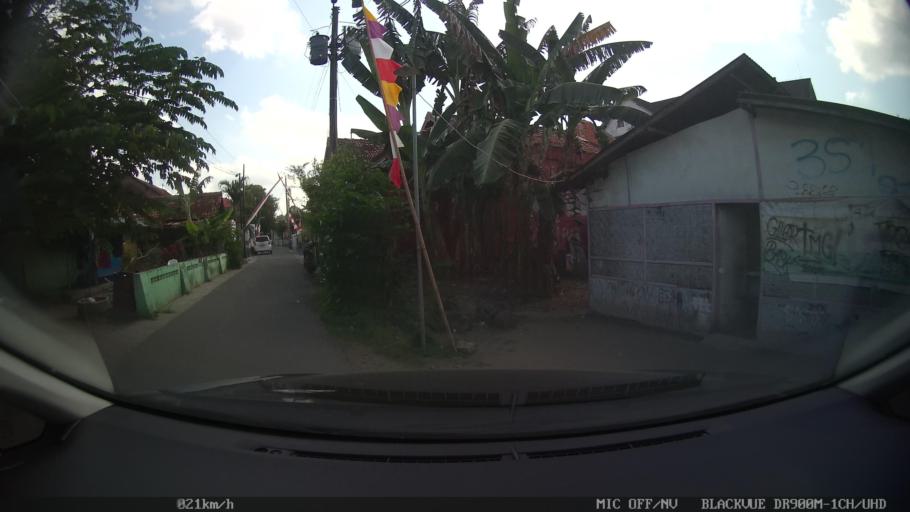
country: ID
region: Daerah Istimewa Yogyakarta
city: Kasihan
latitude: -7.8310
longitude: 110.3704
